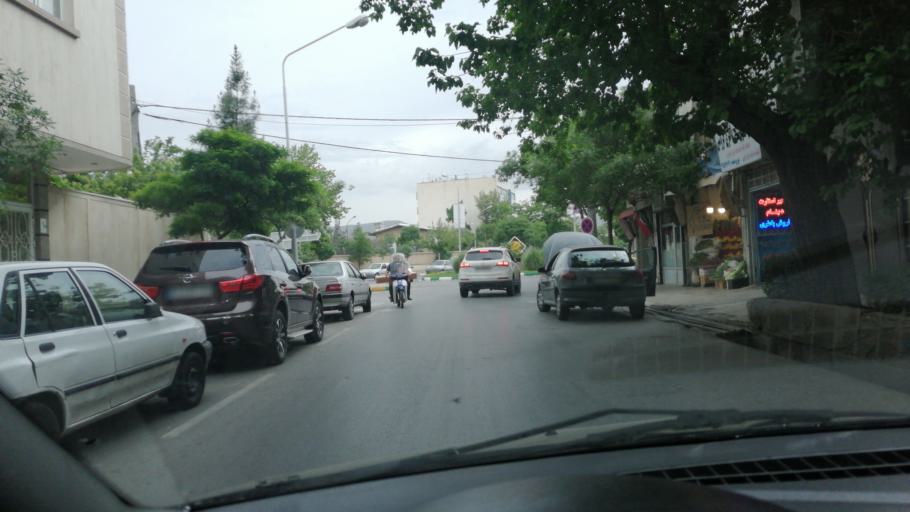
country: IR
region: Razavi Khorasan
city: Mashhad
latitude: 36.2865
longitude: 59.5830
